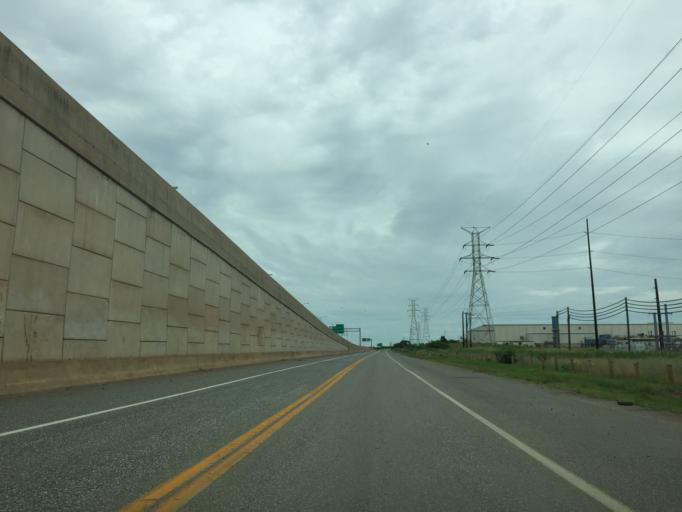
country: US
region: Maryland
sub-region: Baltimore County
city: Dundalk
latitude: 39.2376
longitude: -76.4912
